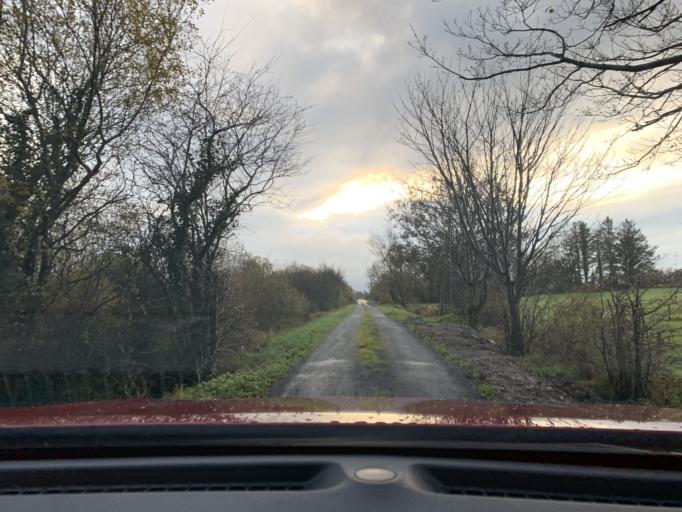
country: IE
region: Connaught
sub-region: Sligo
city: Ballymote
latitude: 54.0323
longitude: -8.5317
